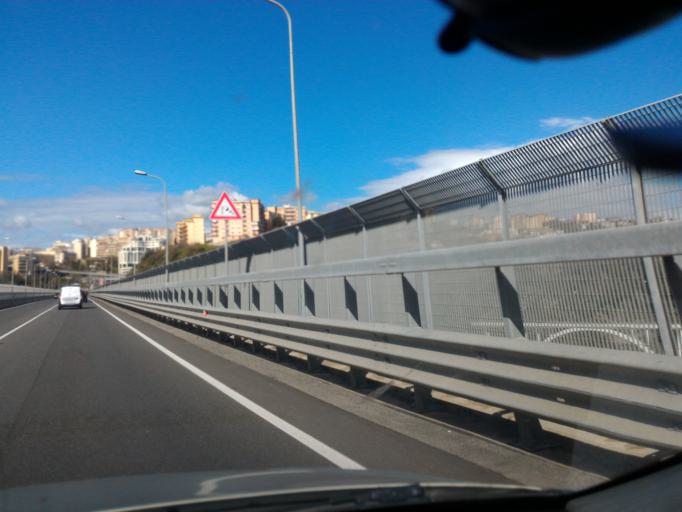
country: IT
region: Calabria
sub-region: Provincia di Catanzaro
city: Siano
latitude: 38.9112
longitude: 16.5969
